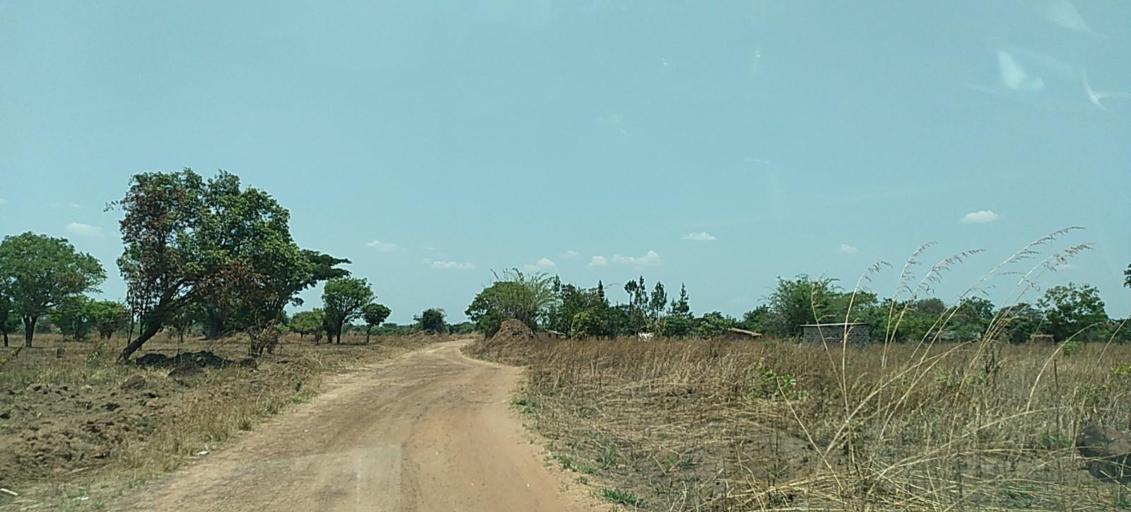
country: ZM
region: Copperbelt
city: Luanshya
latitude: -13.0913
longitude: 28.4064
